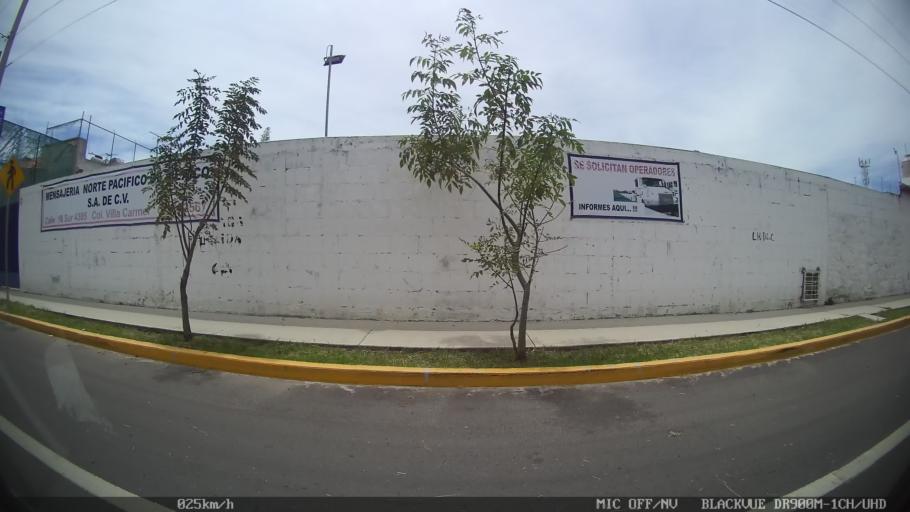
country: MX
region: Puebla
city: Puebla
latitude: 19.0213
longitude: -98.1967
